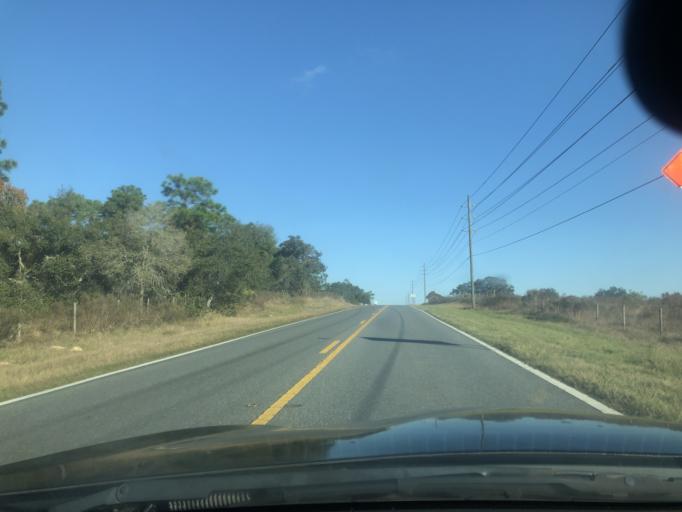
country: US
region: Florida
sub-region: Citrus County
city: Sugarmill Woods
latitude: 28.7640
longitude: -82.5238
